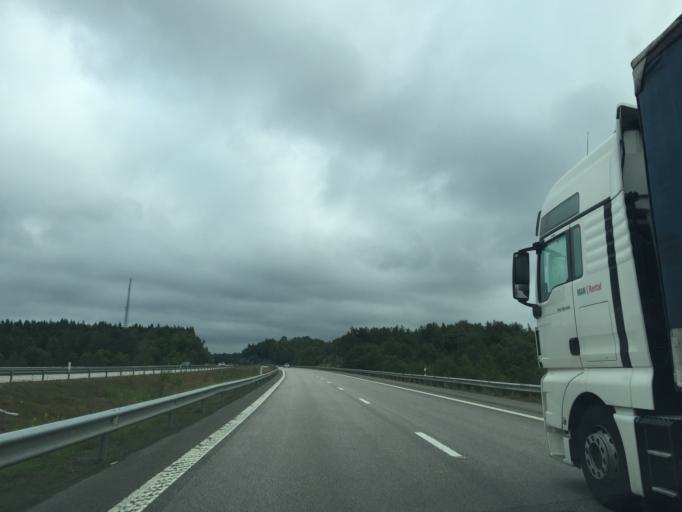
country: SE
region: Halland
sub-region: Kungsbacka Kommun
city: Frillesas
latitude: 57.3480
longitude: 12.2092
